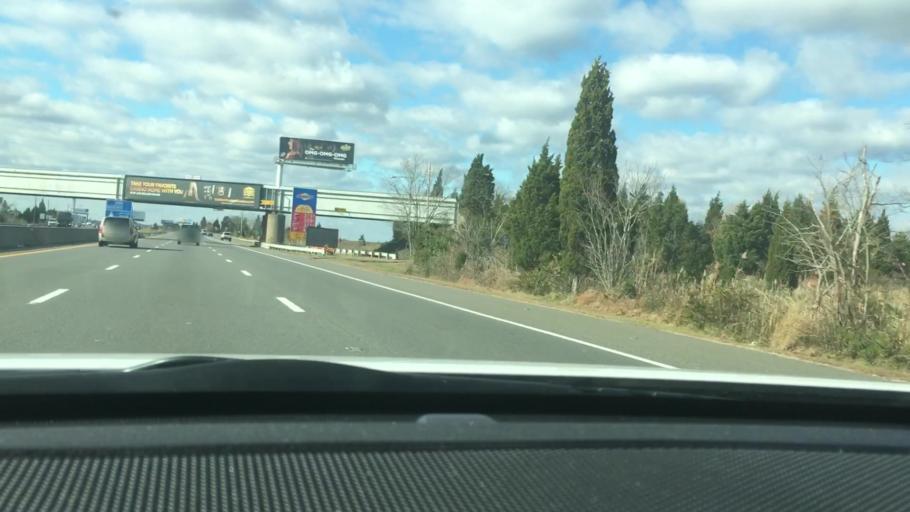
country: US
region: New Jersey
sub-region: Atlantic County
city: Ventnor City
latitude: 39.3768
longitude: -74.4808
